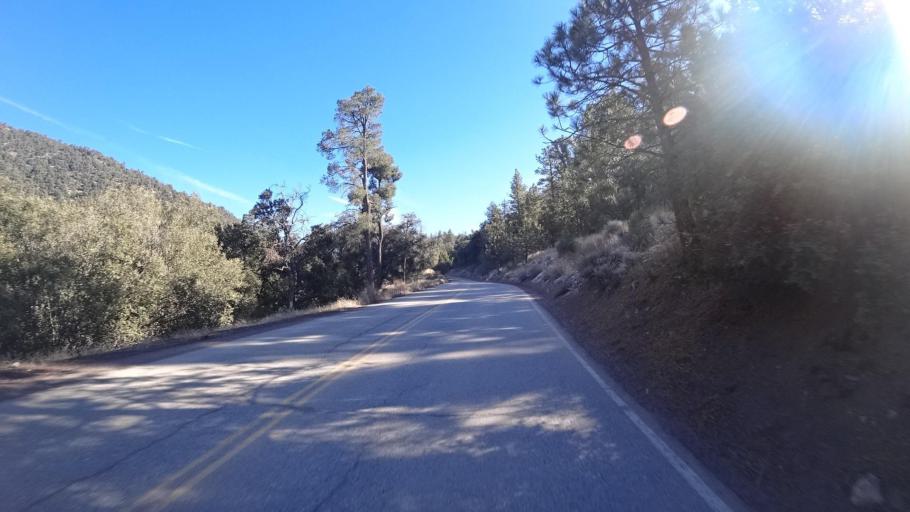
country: US
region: California
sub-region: Kern County
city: Pine Mountain Club
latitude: 34.8517
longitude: -119.1123
